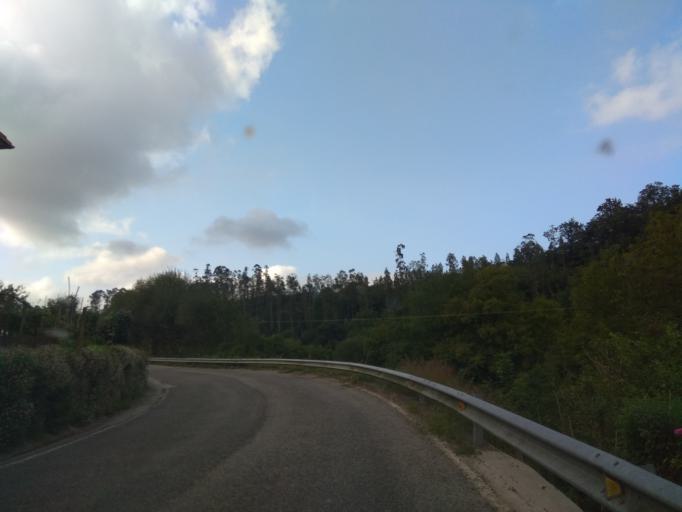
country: ES
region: Cantabria
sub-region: Provincia de Cantabria
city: San Vicente de la Barquera
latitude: 43.3209
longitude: -4.3450
